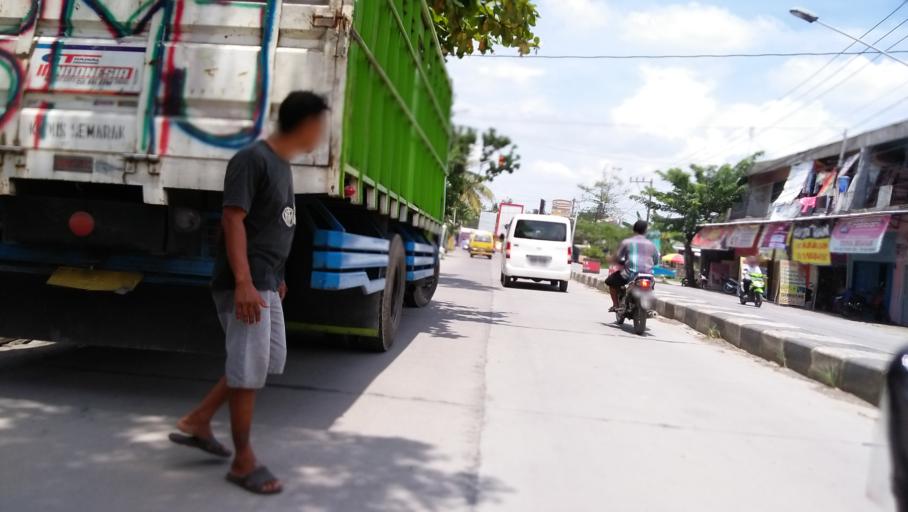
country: ID
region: Central Java
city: Semarang
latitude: -6.9703
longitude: 110.4816
